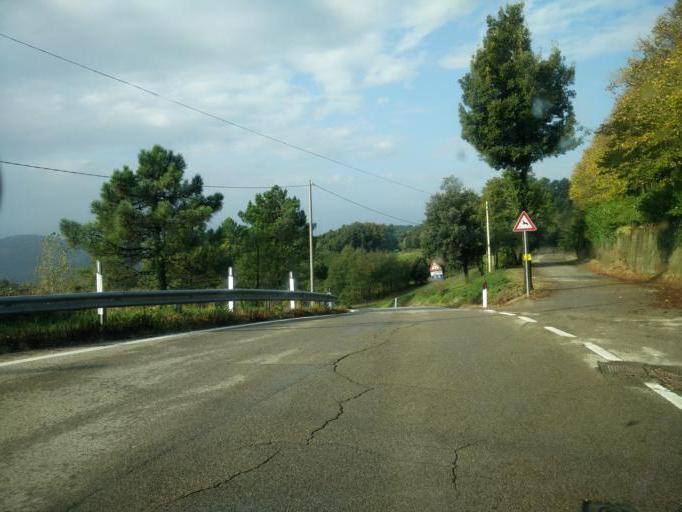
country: IT
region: Tuscany
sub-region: Provincia di Prato
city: Vaiano
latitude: 43.9483
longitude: 11.1013
